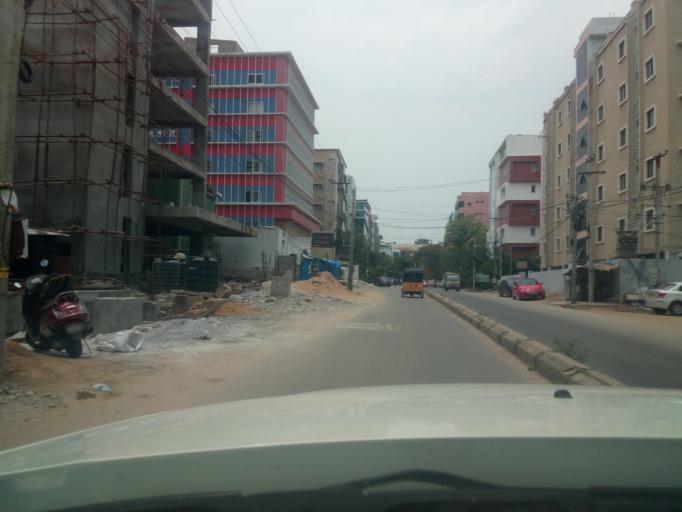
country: IN
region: Telangana
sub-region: Rangareddi
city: Kukatpalli
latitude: 17.4481
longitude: 78.3879
